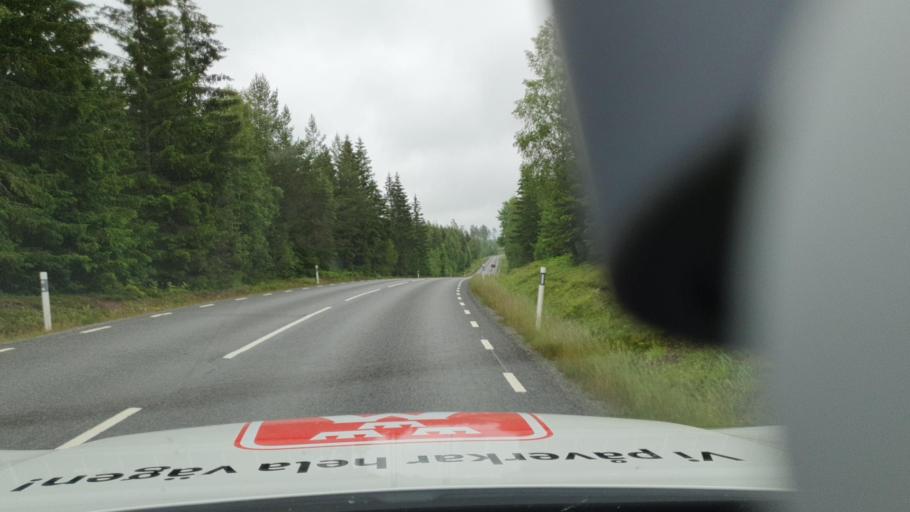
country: SE
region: Vaermland
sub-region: Kristinehamns Kommun
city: Bjorneborg
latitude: 59.2220
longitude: 14.3335
